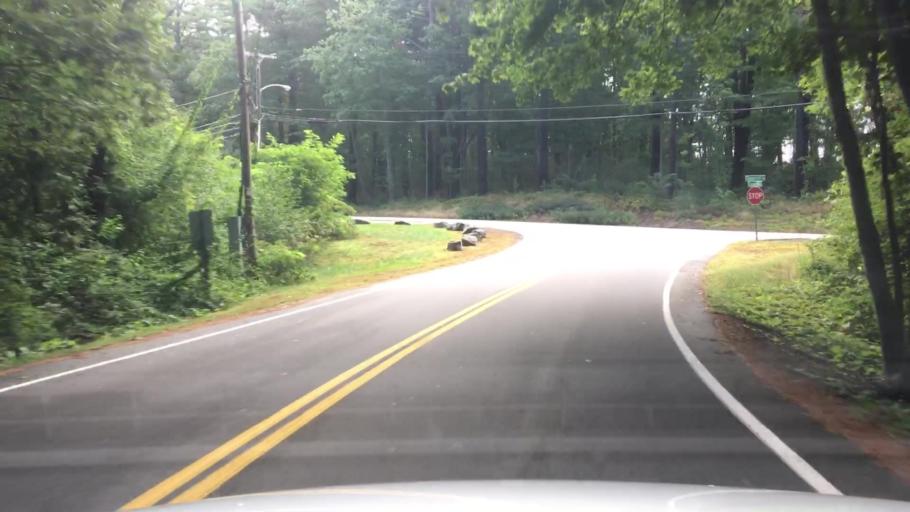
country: US
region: Maine
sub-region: York County
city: Kittery Point
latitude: 43.0833
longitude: -70.7106
